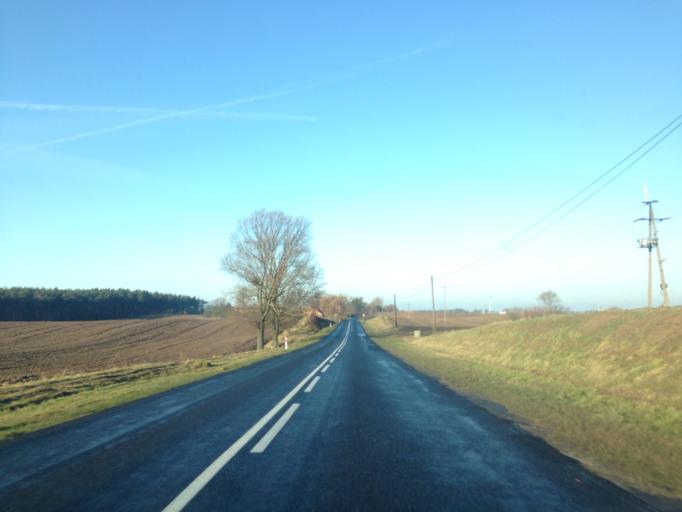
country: PL
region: Kujawsko-Pomorskie
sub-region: Powiat brodnicki
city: Bobrowo
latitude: 53.3290
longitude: 19.2372
